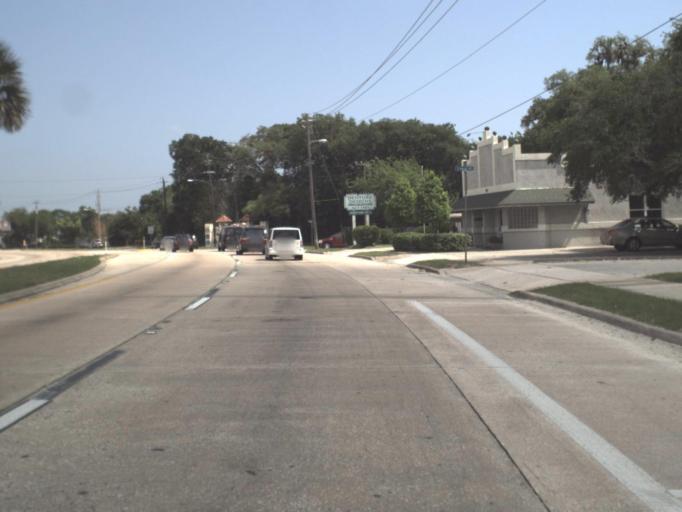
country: US
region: Florida
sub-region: Saint Johns County
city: Saint Augustine
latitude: 29.8862
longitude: -81.3237
